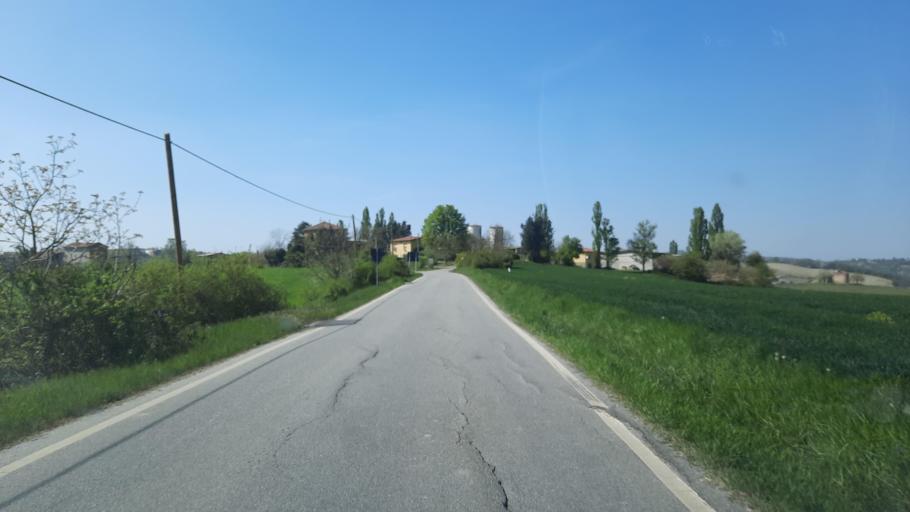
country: IT
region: Piedmont
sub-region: Provincia di Alessandria
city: Vignale Monferrato
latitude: 45.0107
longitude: 8.3852
